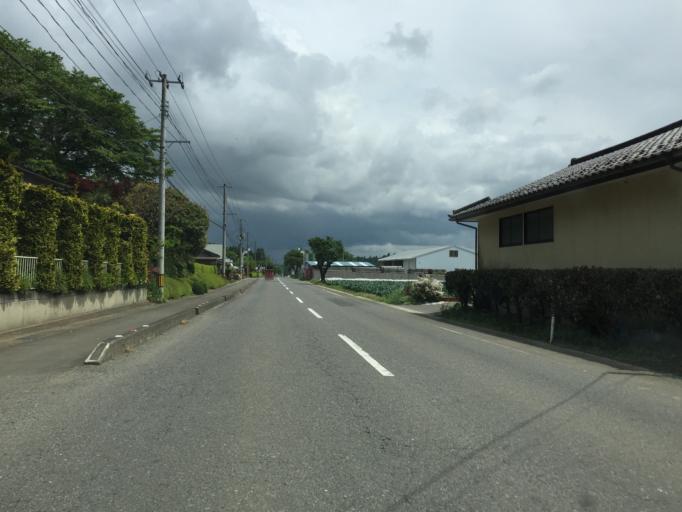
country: JP
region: Fukushima
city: Ishikawa
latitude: 37.1109
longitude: 140.3312
